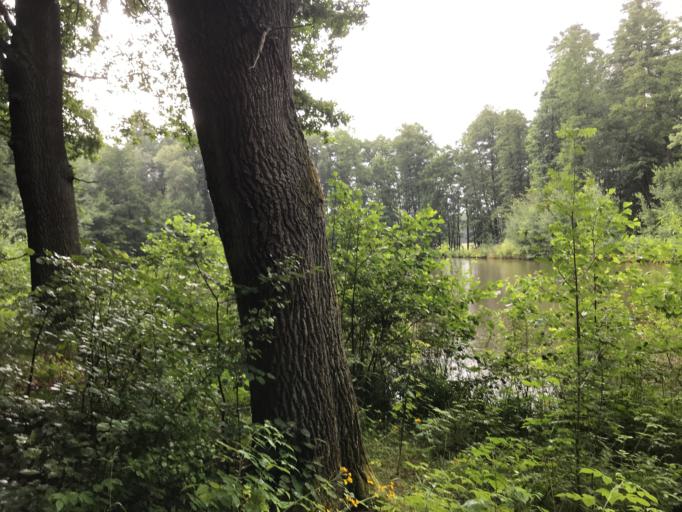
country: CZ
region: Jihocesky
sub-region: Okres Jindrichuv Hradec
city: Trebon
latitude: 48.9829
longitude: 14.7913
